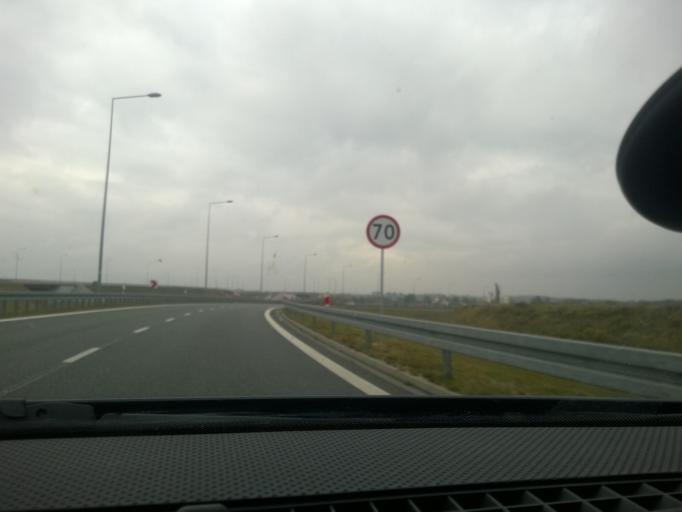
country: PL
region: Lodz Voivodeship
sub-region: Powiat zgierski
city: Strykow
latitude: 51.8888
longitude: 19.6388
